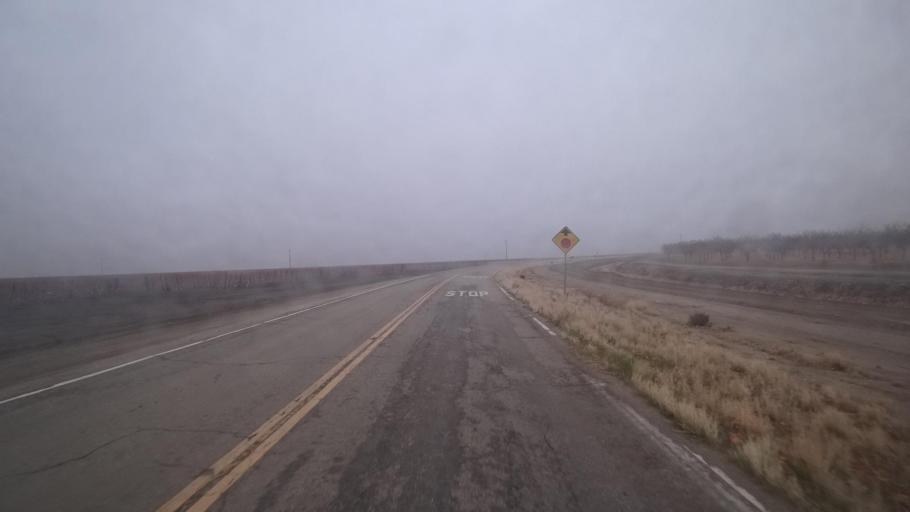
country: US
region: California
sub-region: Kern County
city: Buttonwillow
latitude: 35.4205
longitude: -119.5206
